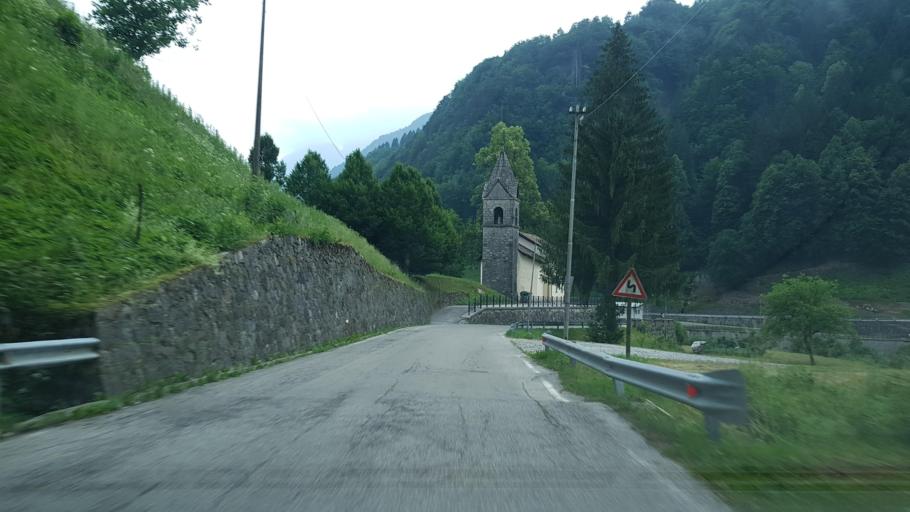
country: IT
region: Friuli Venezia Giulia
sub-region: Provincia di Udine
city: Pontebba
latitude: 46.5103
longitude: 13.3028
